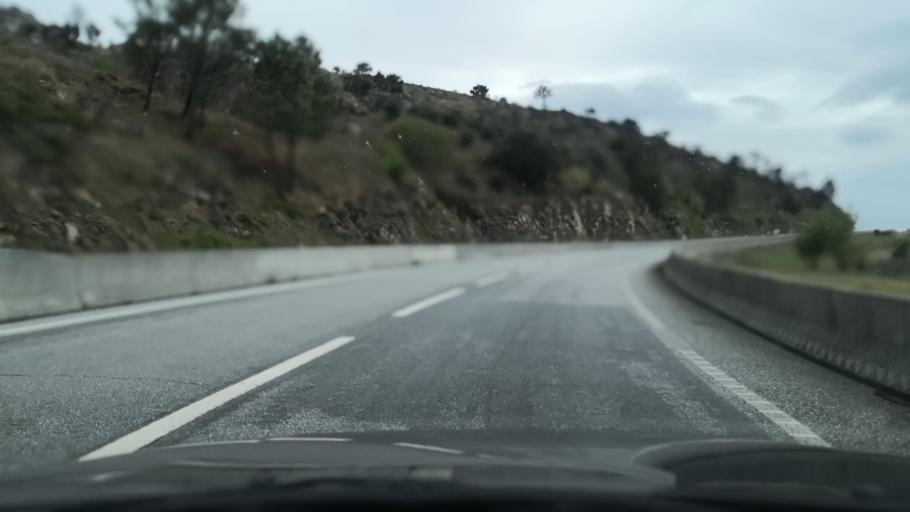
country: PT
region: Guarda
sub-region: Guarda
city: Guarda
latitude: 40.6011
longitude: -7.2751
